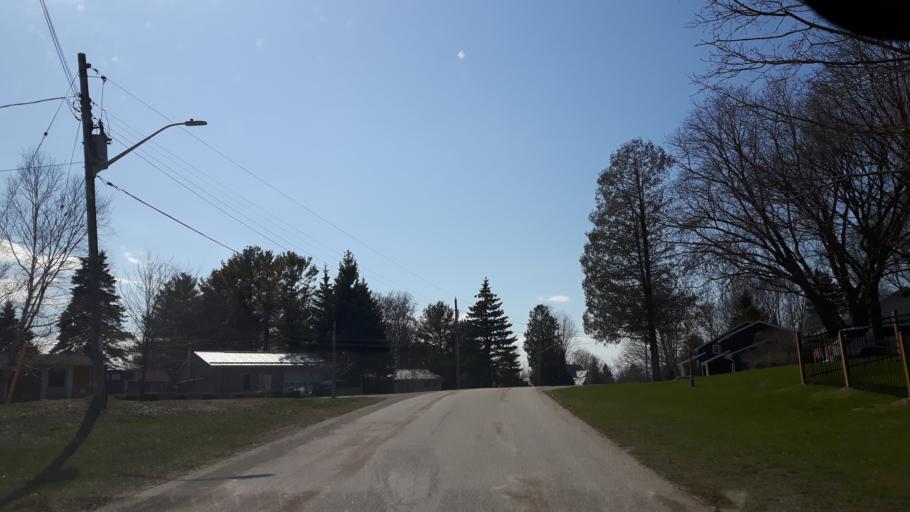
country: CA
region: Ontario
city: Bluewater
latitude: 43.5607
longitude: -81.6926
